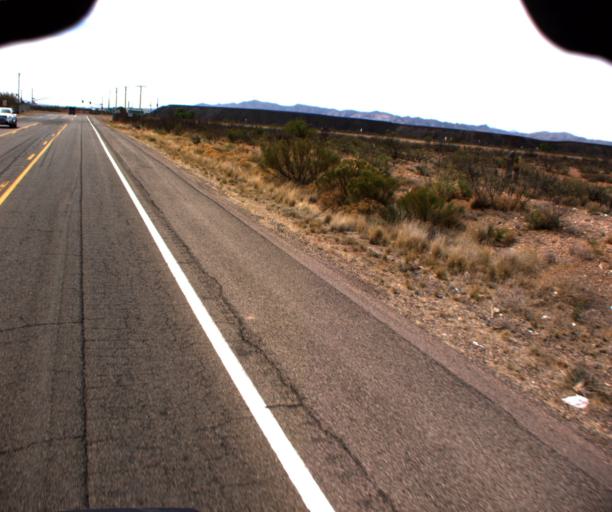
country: US
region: Arizona
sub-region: Cochise County
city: Pirtleville
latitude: 31.3550
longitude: -109.5795
